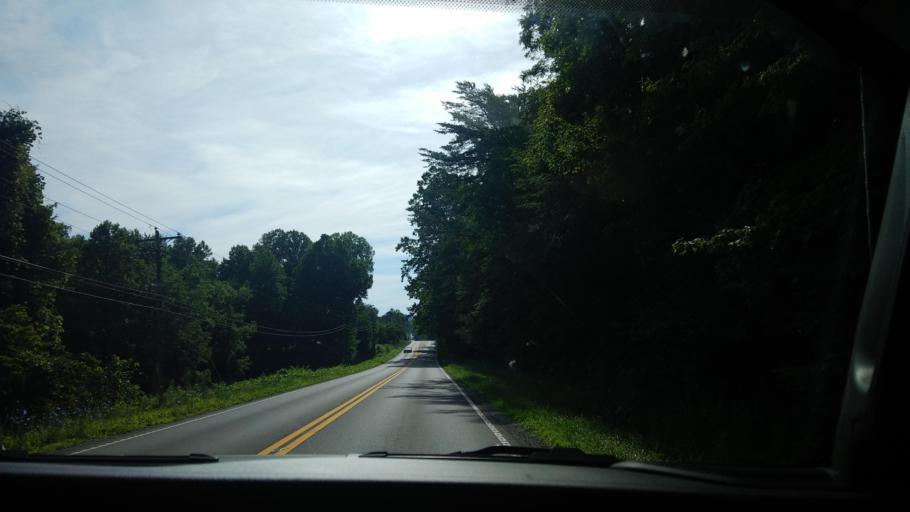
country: US
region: Tennessee
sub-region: Sevier County
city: Gatlinburg
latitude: 35.7592
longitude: -83.3488
